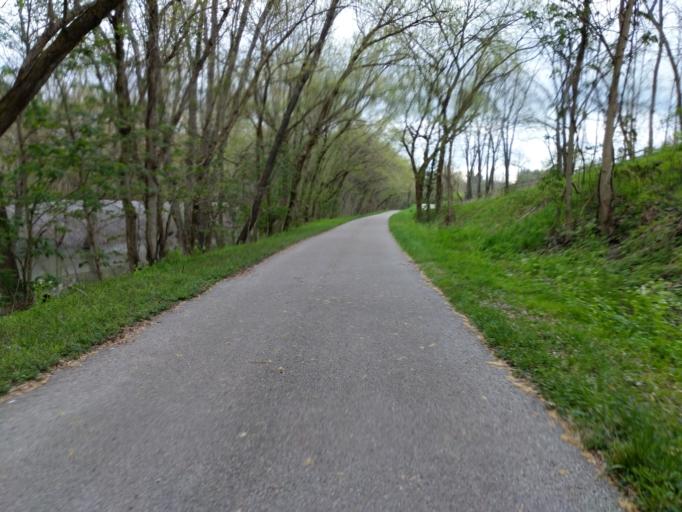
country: US
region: Ohio
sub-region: Athens County
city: Chauncey
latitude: 39.3855
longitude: -82.1188
